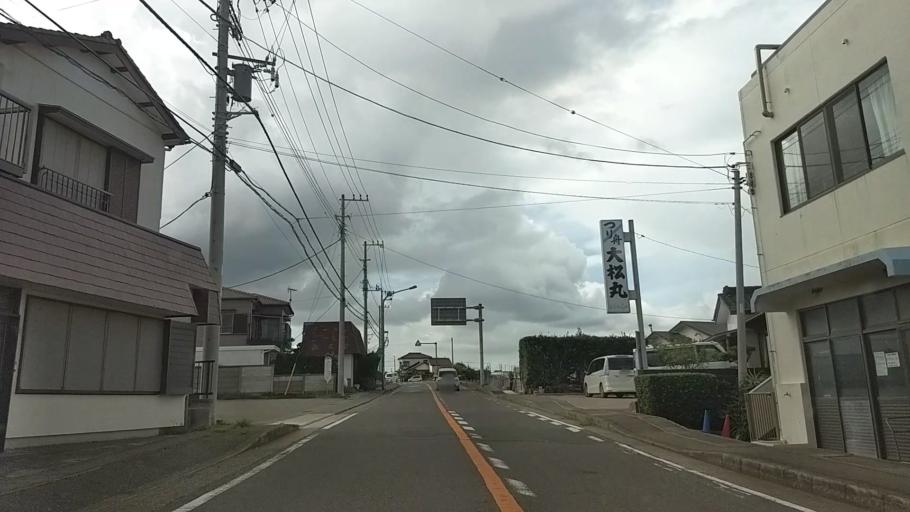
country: JP
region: Kanagawa
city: Miura
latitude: 35.1468
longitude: 139.6698
